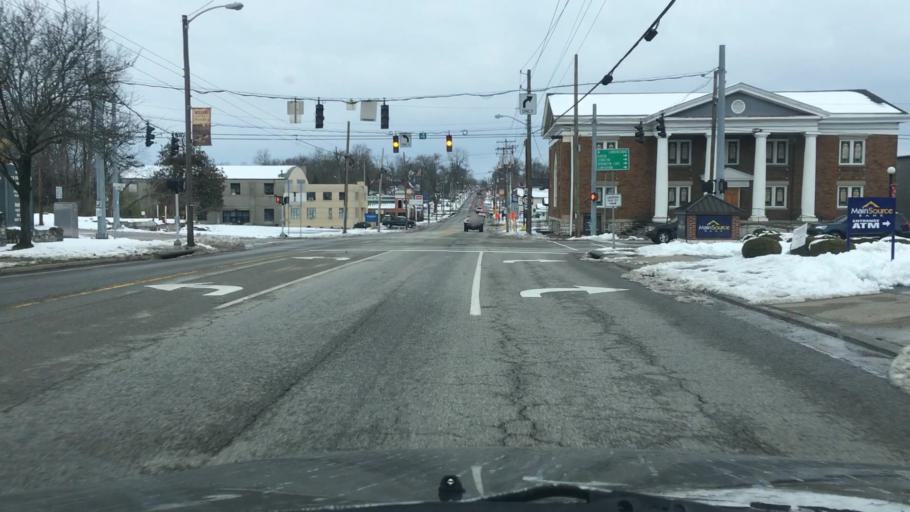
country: US
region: Kentucky
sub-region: Mercer County
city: Harrodsburg
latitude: 37.7621
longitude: -84.8456
